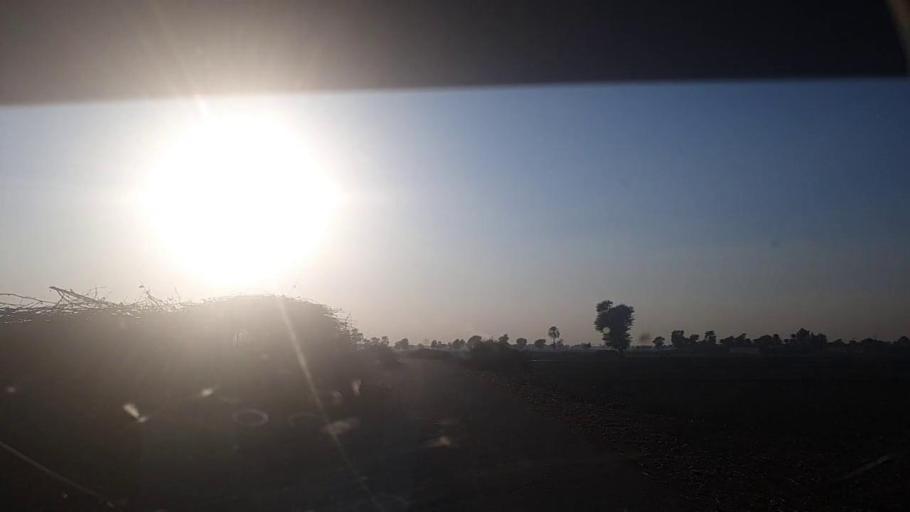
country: PK
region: Sindh
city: Hingorja
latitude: 27.2220
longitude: 68.4086
